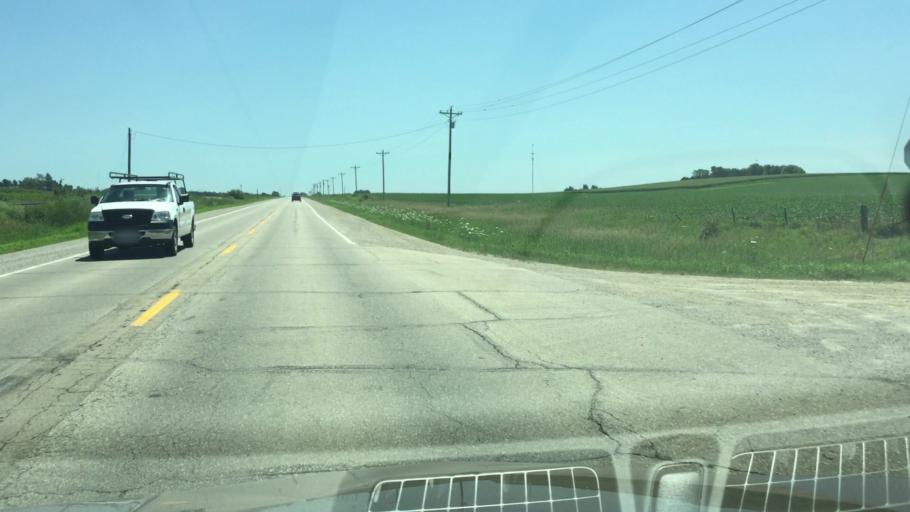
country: US
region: Iowa
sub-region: Cedar County
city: Mechanicsville
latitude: 41.9110
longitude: -91.2885
